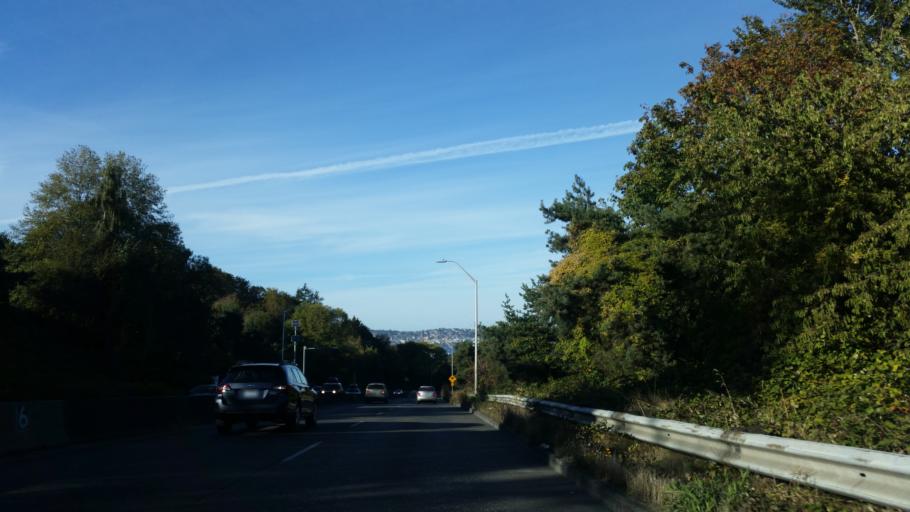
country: US
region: Washington
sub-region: King County
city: White Center
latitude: 47.5686
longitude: -122.3730
